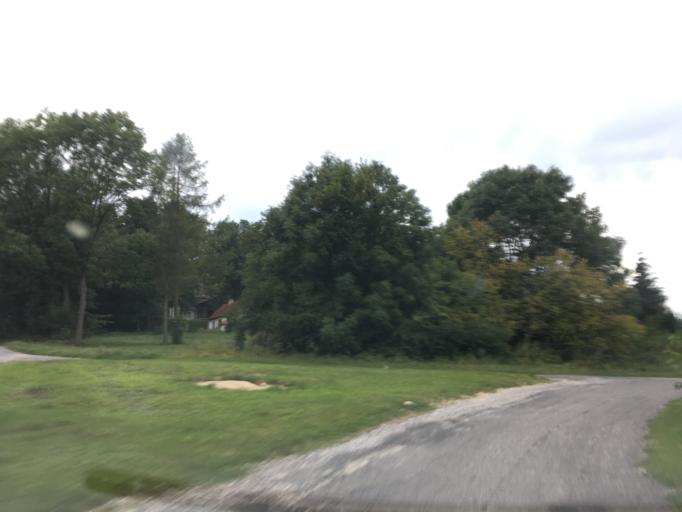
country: PL
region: Lodz Voivodeship
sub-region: Powiat piotrkowski
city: Reczno
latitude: 51.1394
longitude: 19.8632
